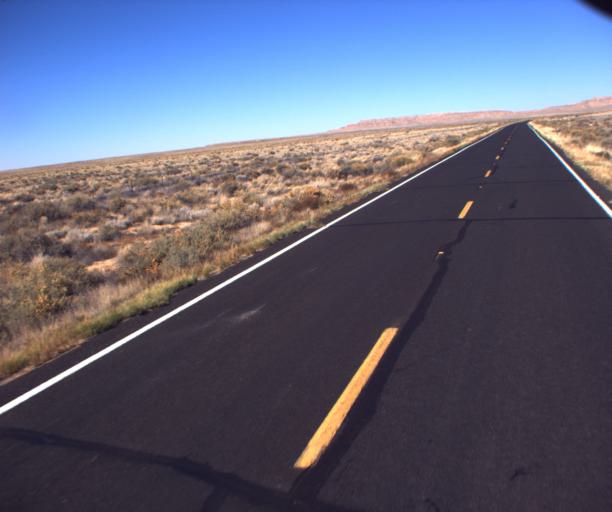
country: US
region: Arizona
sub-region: Navajo County
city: First Mesa
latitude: 35.7255
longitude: -110.5167
